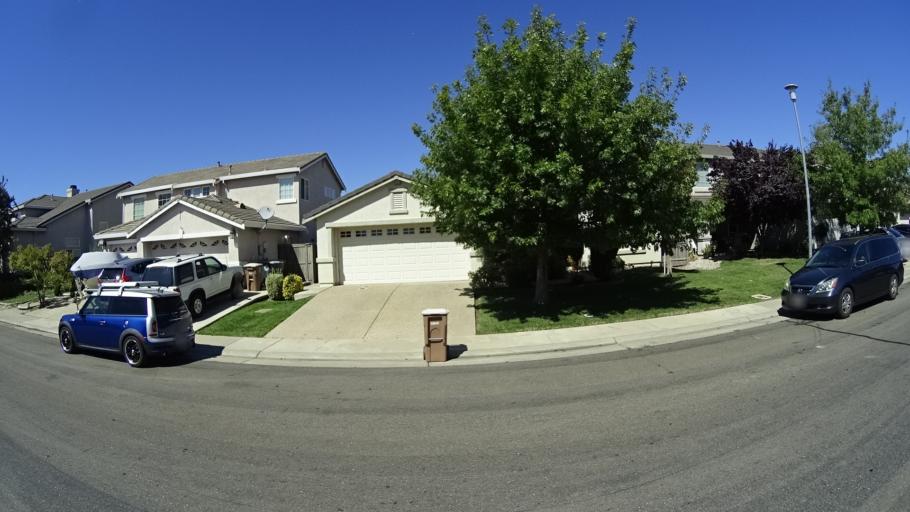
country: US
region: California
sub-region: Sacramento County
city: Elk Grove
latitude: 38.4063
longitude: -121.3471
